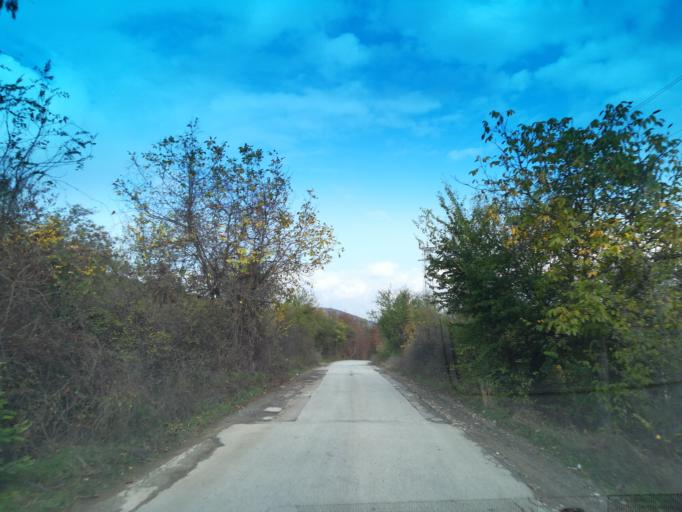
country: BG
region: Stara Zagora
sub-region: Obshtina Nikolaevo
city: Elkhovo
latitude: 42.3325
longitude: 25.4045
